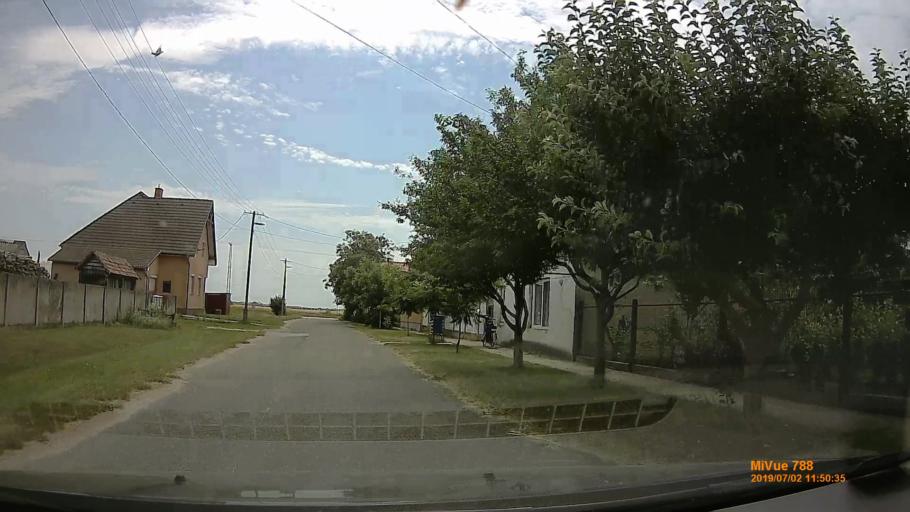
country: HU
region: Gyor-Moson-Sopron
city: Janossomorja
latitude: 47.8468
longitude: 17.1739
